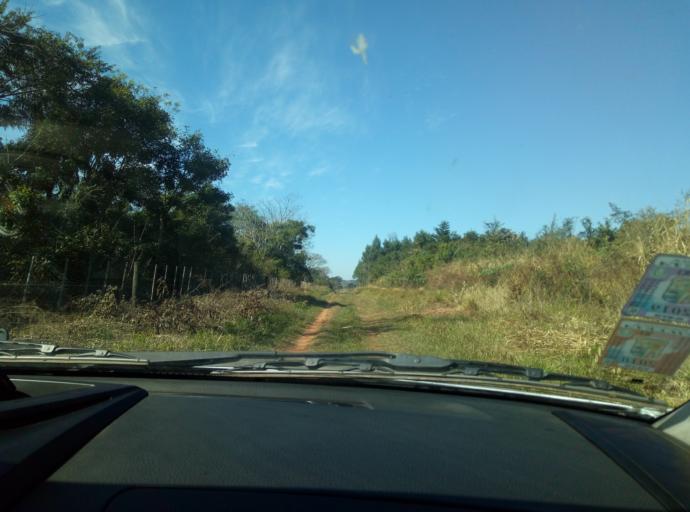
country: PY
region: Caaguazu
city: Carayao
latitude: -25.1760
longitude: -56.3048
